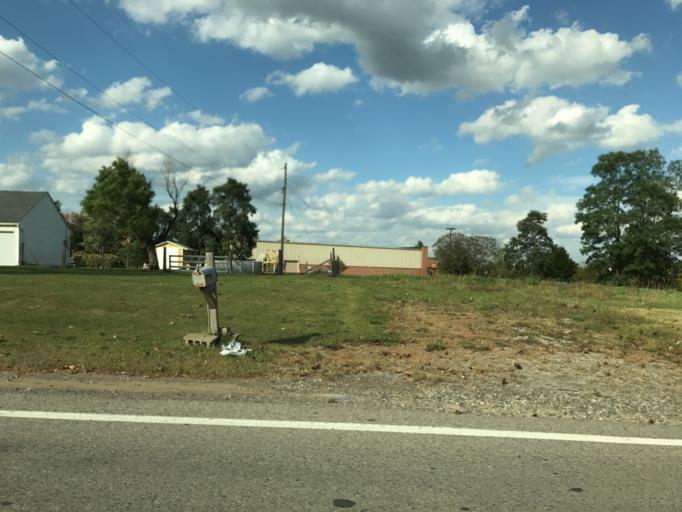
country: US
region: Michigan
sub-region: Oakland County
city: Wixom
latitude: 42.4962
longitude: -83.5444
